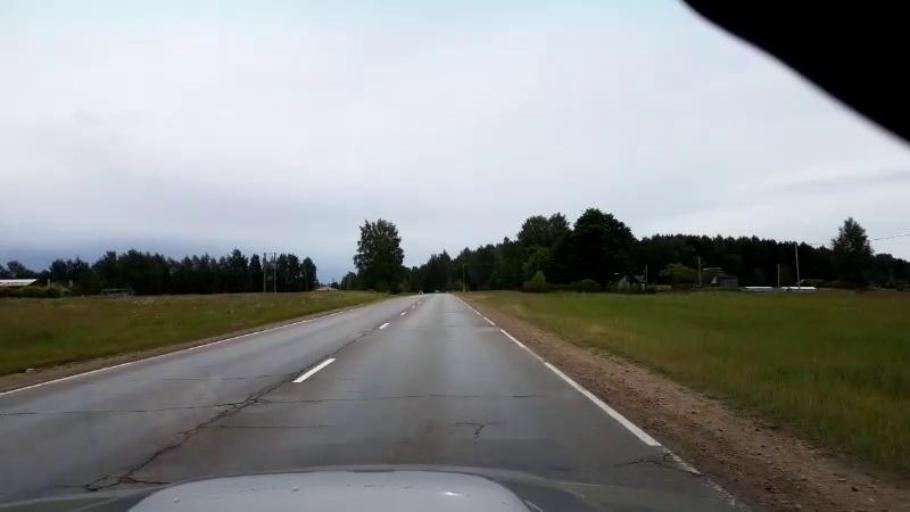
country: LV
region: Kekava
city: Kekava
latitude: 56.8007
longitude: 24.2540
